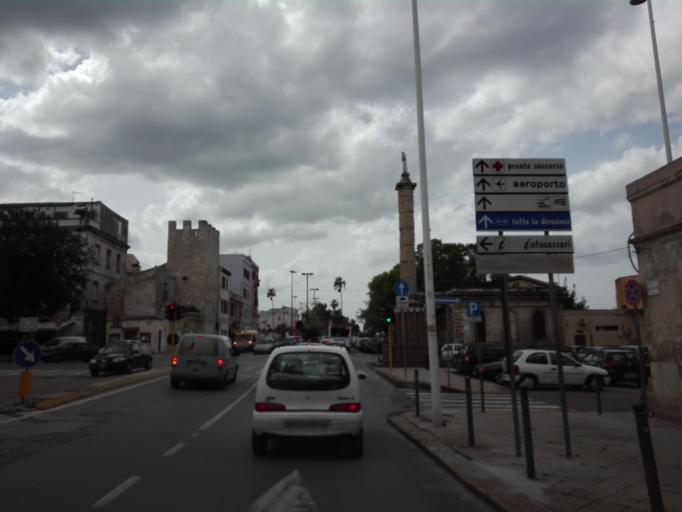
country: IT
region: Sardinia
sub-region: Provincia di Sassari
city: Sassari
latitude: 40.7306
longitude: 8.5563
